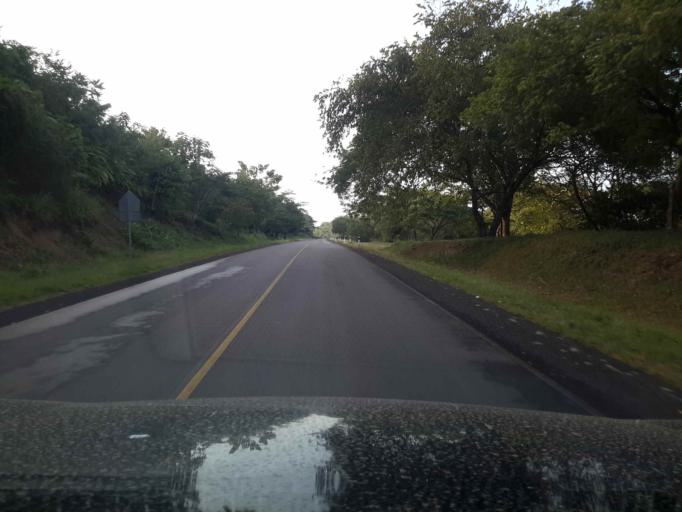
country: NI
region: Rio San Juan
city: San Miguelito
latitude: 11.3778
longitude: -84.7837
